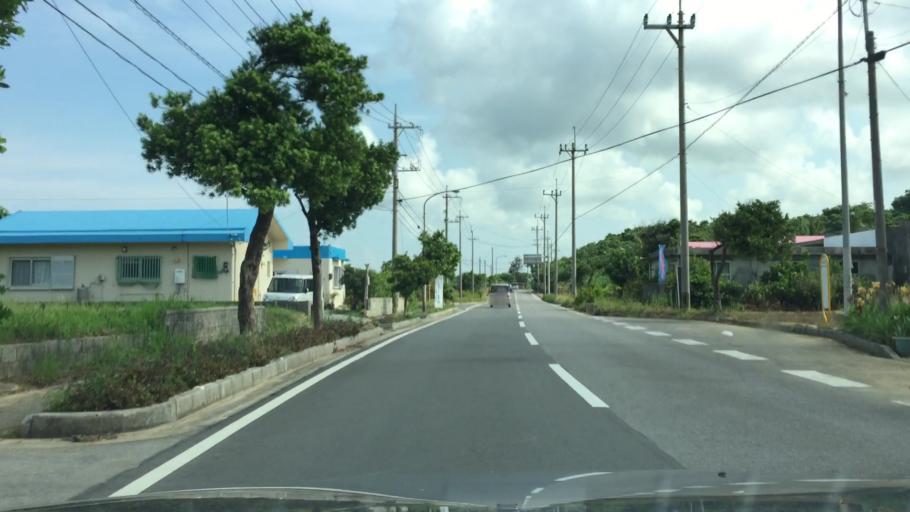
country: JP
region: Okinawa
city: Ishigaki
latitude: 24.4628
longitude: 124.2504
